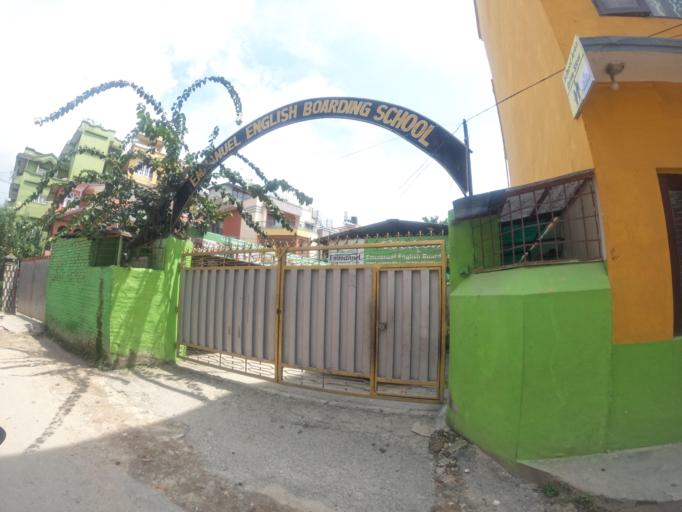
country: NP
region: Central Region
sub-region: Bagmati Zone
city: Bhaktapur
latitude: 27.6745
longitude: 85.3725
